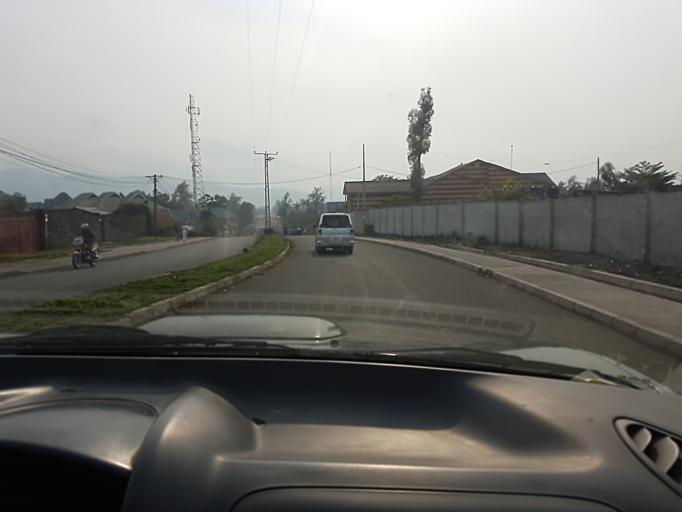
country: CD
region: Nord Kivu
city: Goma
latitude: -1.6874
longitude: 29.2293
